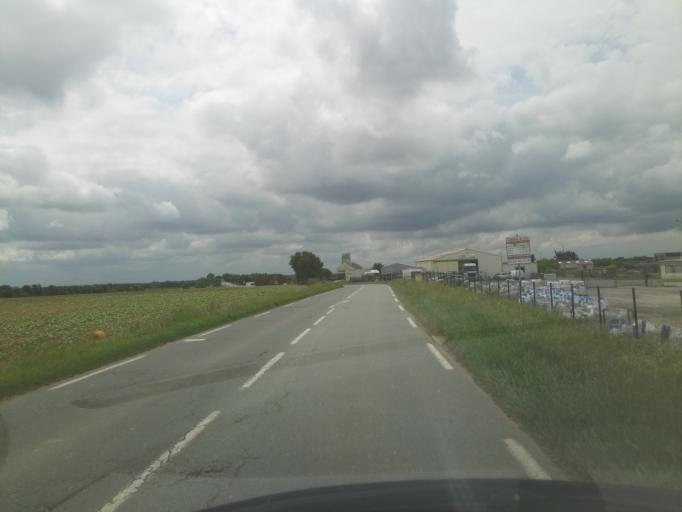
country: FR
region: Poitou-Charentes
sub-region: Departement de la Charente-Maritime
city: Saint-Jean-de-Liversay
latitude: 46.2322
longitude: -0.8807
